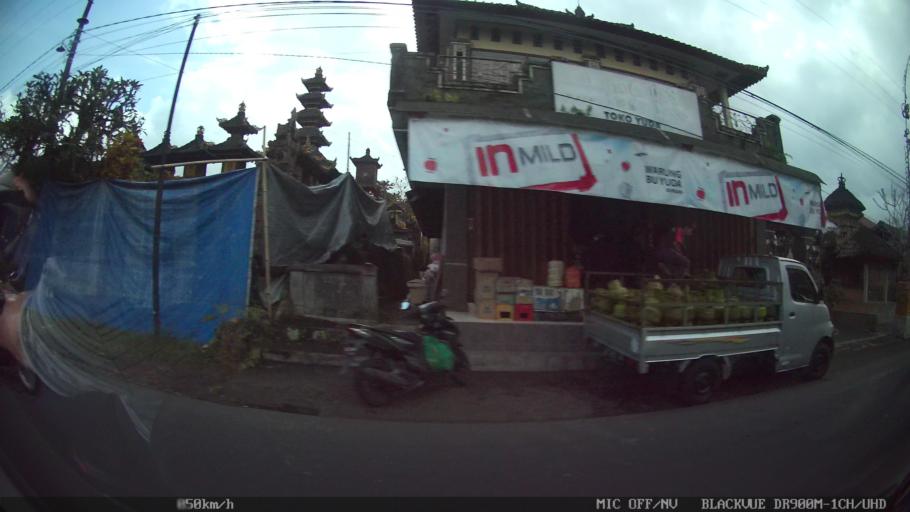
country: ID
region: Bali
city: Pohgending Kawan
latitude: -8.4556
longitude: 115.1386
